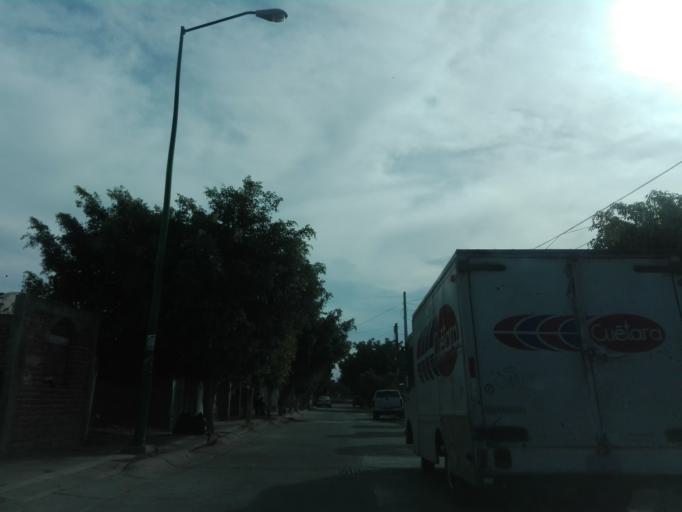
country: MX
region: Guanajuato
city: Leon
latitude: 21.1936
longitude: -101.6758
